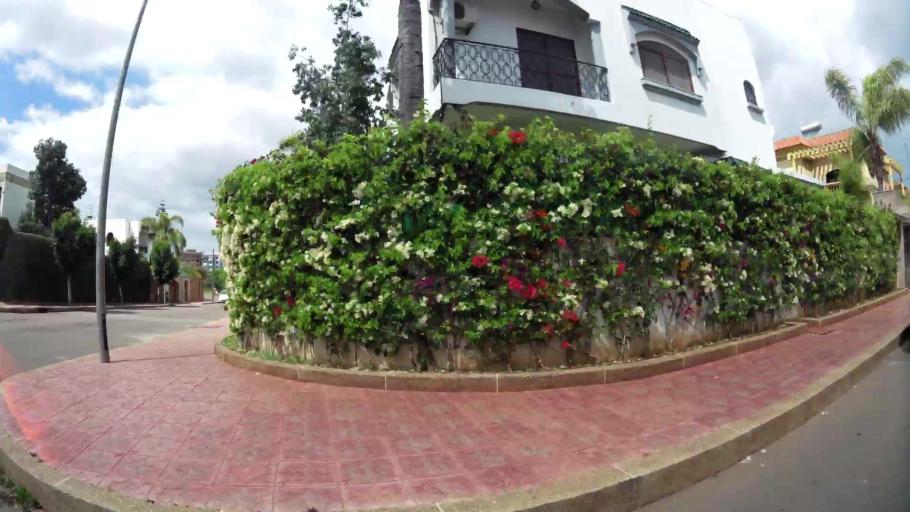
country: MA
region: Grand Casablanca
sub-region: Casablanca
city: Casablanca
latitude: 33.5601
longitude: -7.6226
